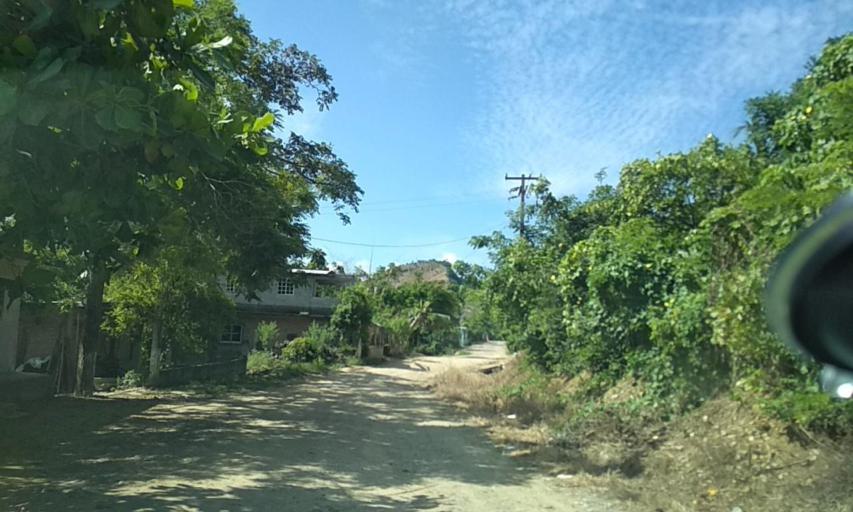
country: MX
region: Veracruz
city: Cazones de Herrera
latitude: 20.6475
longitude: -97.3044
